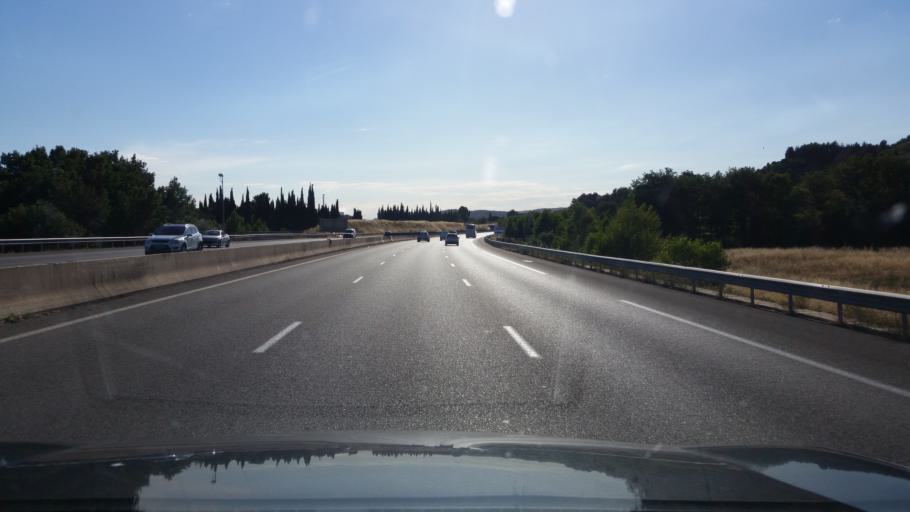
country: FR
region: Provence-Alpes-Cote d'Azur
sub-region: Departement des Bouches-du-Rhone
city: Chateauneuf-le-Rouge
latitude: 43.4796
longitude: 5.5838
